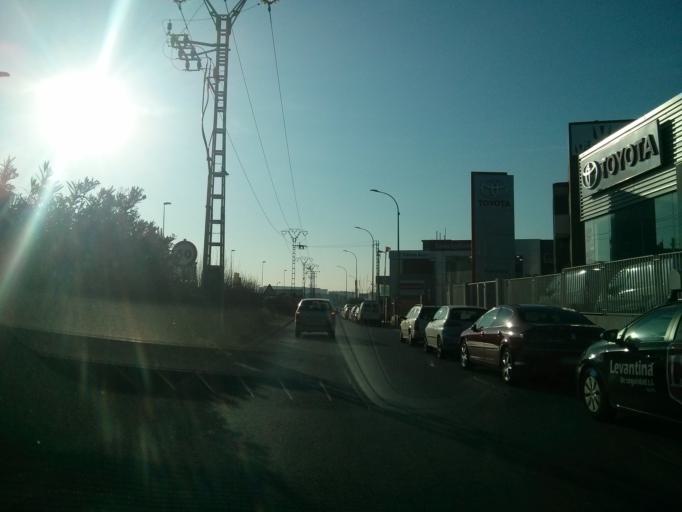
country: ES
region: Valencia
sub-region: Provincia de Valencia
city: Manises
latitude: 39.5184
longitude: -0.4609
